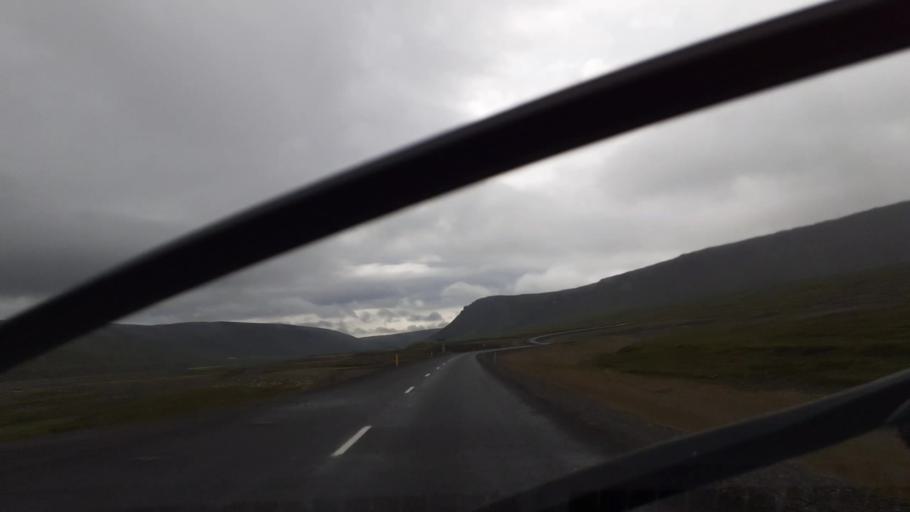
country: IS
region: East
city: Egilsstadir
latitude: 65.6287
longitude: -15.0650
